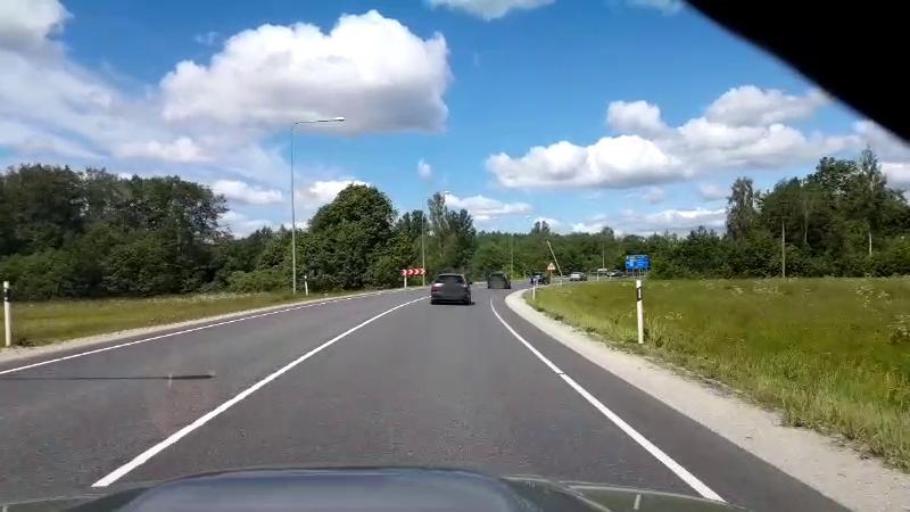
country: EE
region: Paernumaa
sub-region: Sauga vald
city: Sauga
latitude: 58.4460
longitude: 24.4984
